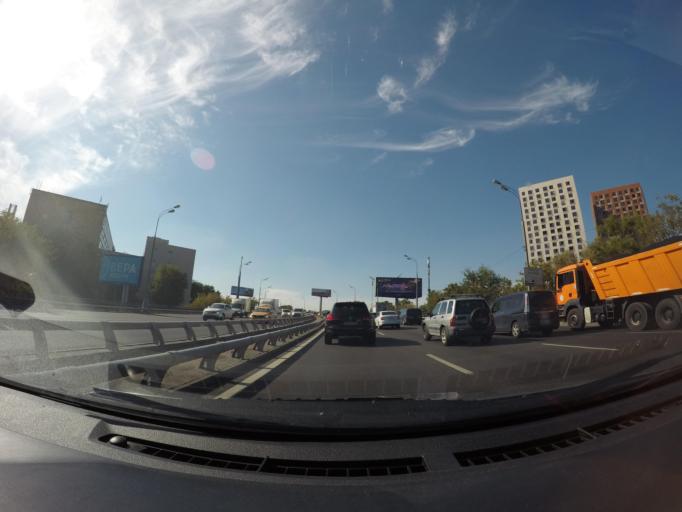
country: RU
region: Moscow
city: Sokol'niki
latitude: 55.7929
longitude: 37.6534
